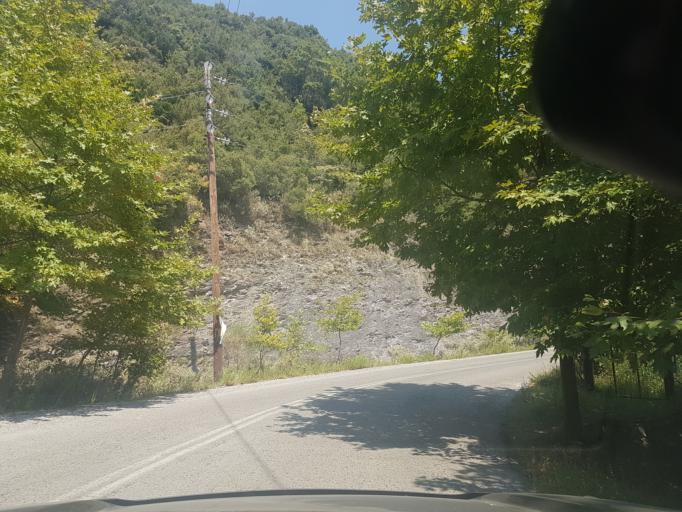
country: GR
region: Central Greece
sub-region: Nomos Evvoias
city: Yimnon
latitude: 38.6361
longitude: 23.8907
